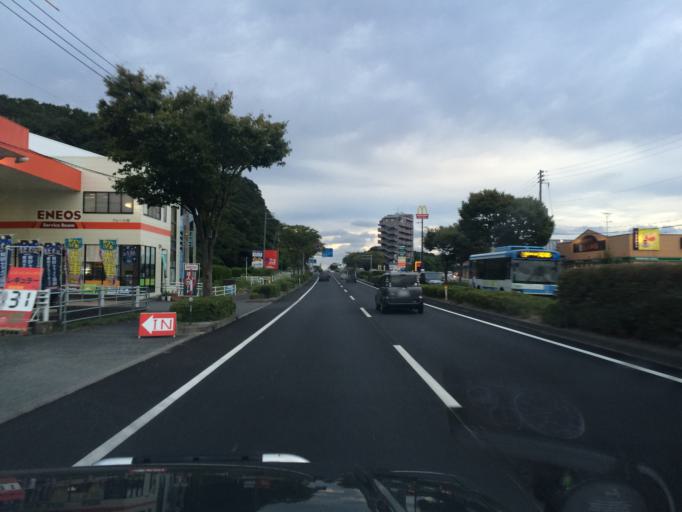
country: JP
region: Tottori
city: Tottori
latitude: 35.4943
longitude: 134.2030
